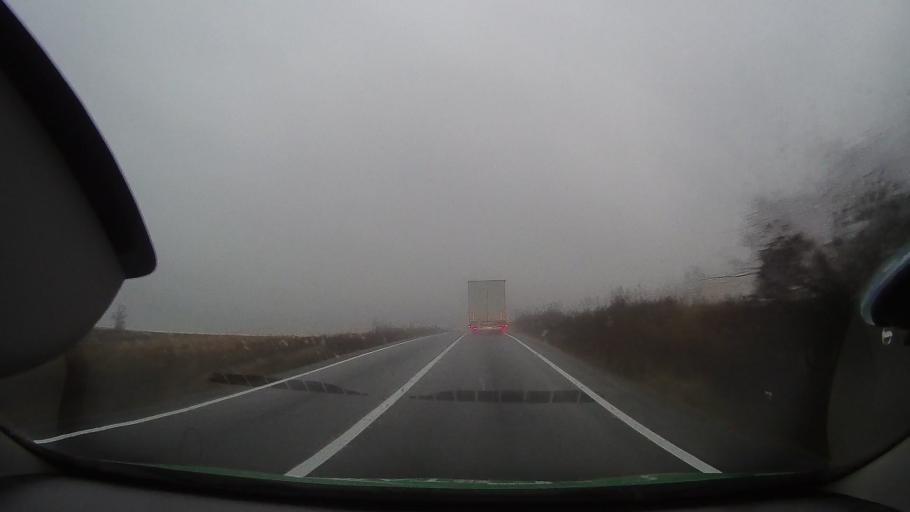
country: RO
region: Bihor
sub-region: Comuna Olcea
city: Calacea
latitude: 46.6537
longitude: 21.9596
